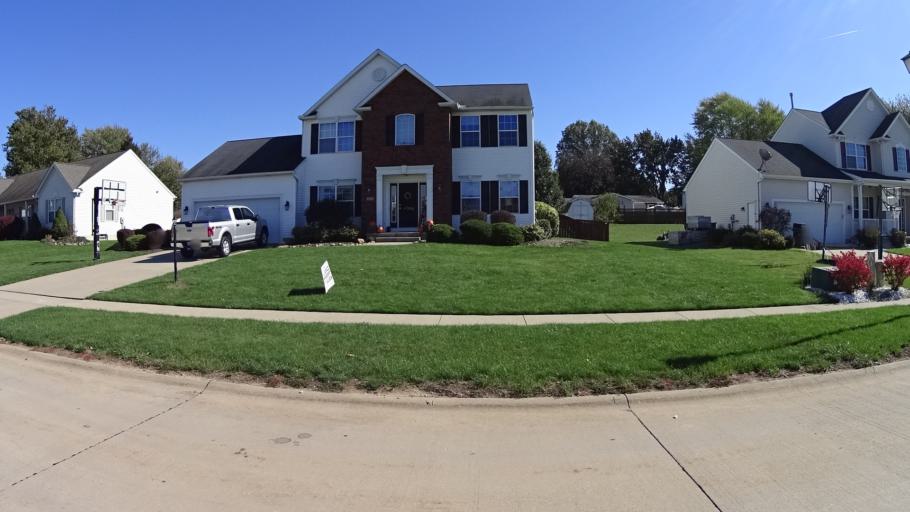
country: US
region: Ohio
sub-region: Lorain County
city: Amherst
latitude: 41.3874
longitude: -82.2199
